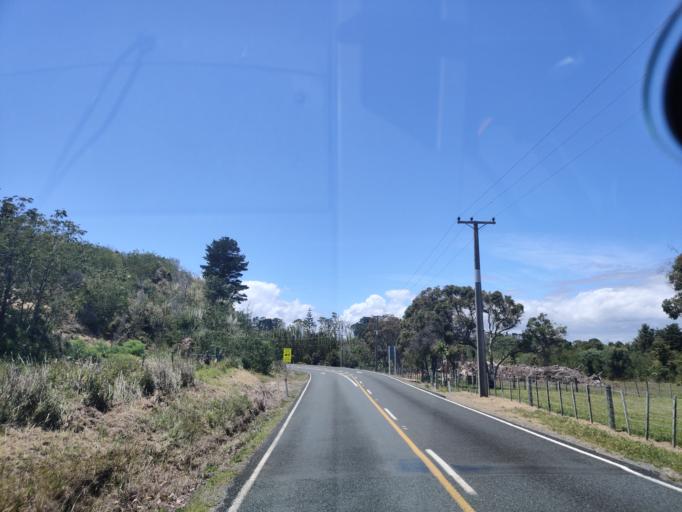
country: NZ
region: Northland
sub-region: Far North District
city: Kaitaia
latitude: -35.0271
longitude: 173.1998
